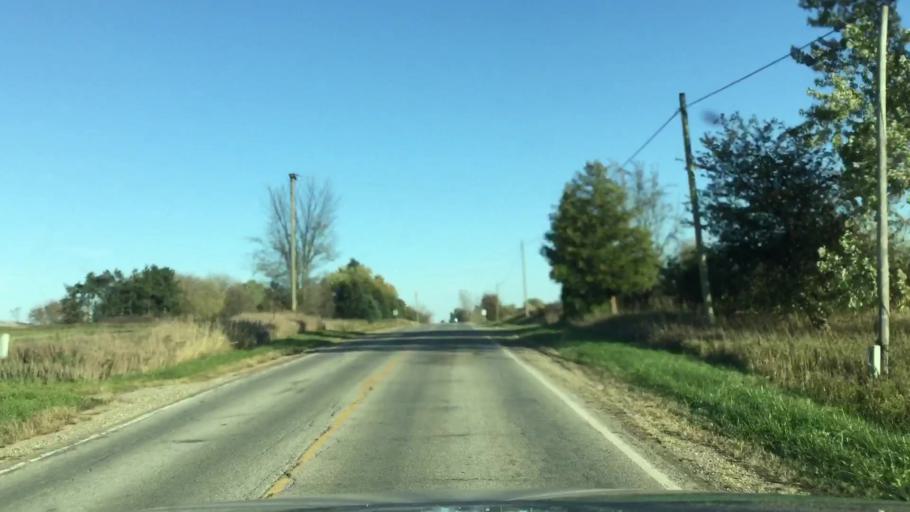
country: US
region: Michigan
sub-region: Lapeer County
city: North Branch
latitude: 43.3126
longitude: -83.1960
